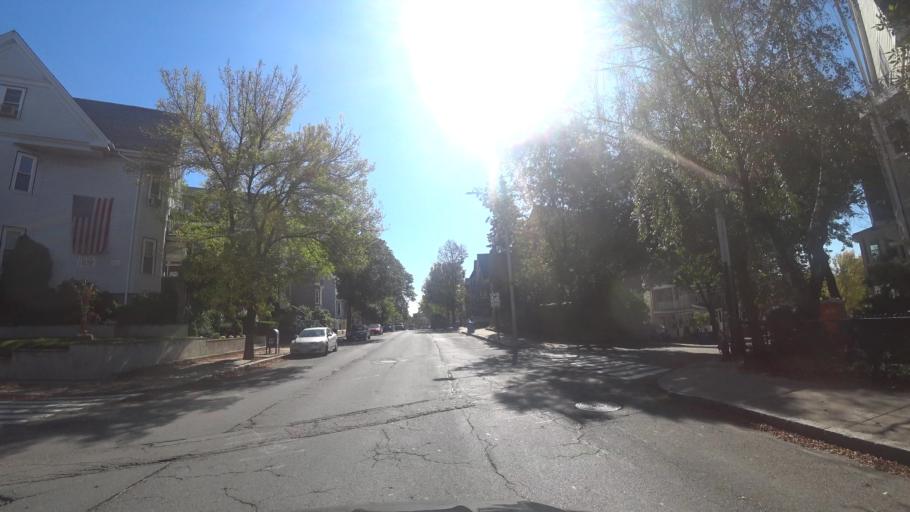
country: US
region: Massachusetts
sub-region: Middlesex County
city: Somerville
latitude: 42.3945
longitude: -71.1022
